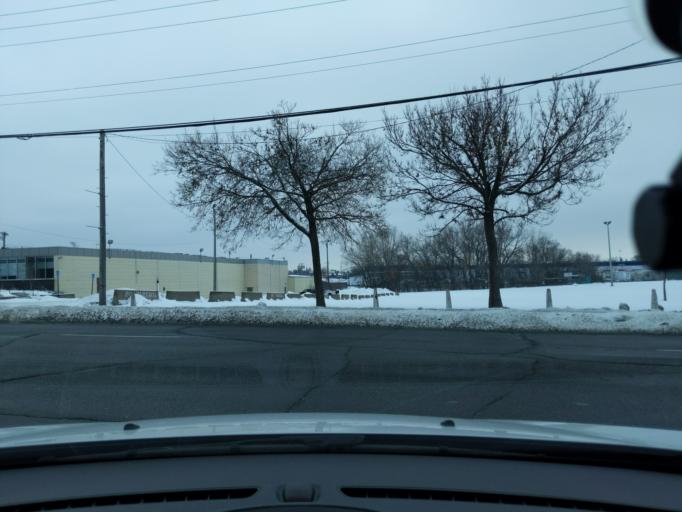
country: US
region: Minnesota
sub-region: Ramsey County
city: Falcon Heights
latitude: 44.9774
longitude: -93.1706
